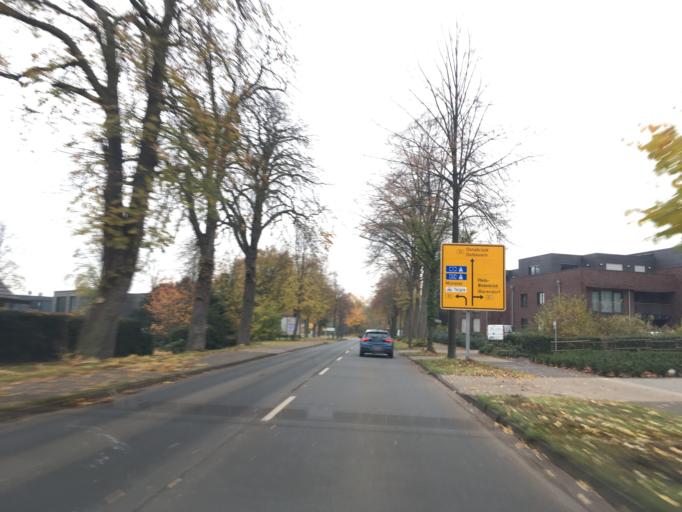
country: DE
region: North Rhine-Westphalia
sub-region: Regierungsbezirk Munster
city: Telgte
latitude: 51.9880
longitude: 7.7967
